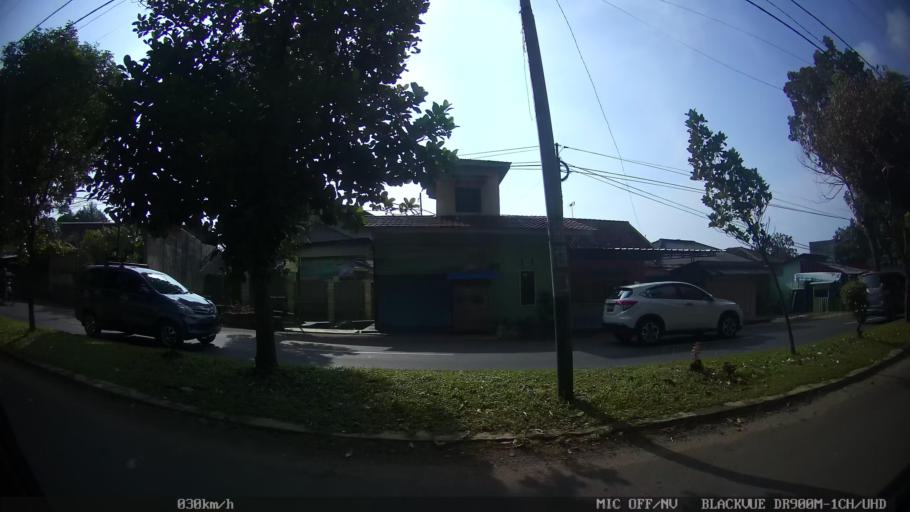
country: ID
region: Lampung
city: Bandarlampung
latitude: -5.4238
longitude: 105.2472
